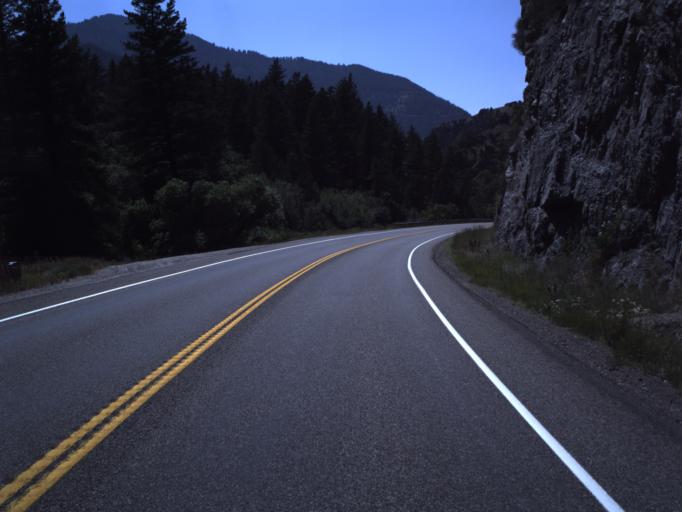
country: US
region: Utah
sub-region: Cache County
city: North Logan
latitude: 41.7771
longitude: -111.6483
